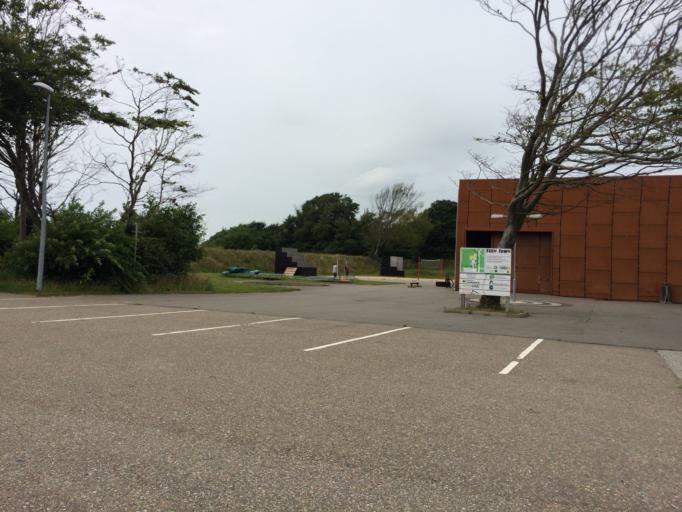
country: DK
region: Central Jutland
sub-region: Holstebro Kommune
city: Ulfborg
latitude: 56.2785
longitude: 8.3202
